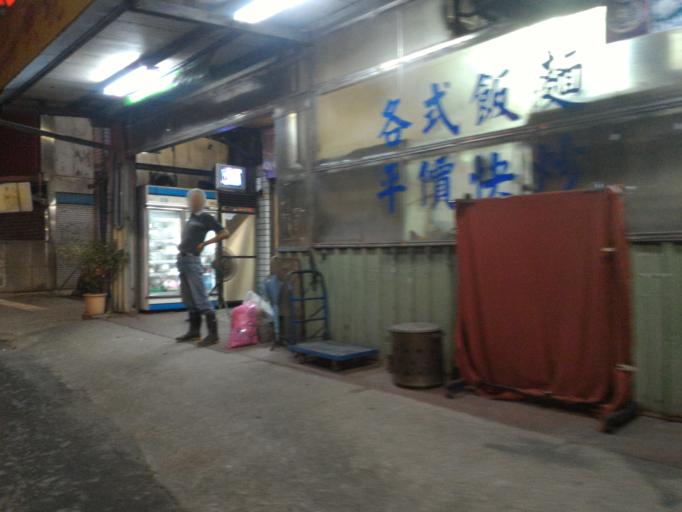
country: TW
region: Taipei
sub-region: Taipei
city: Banqiao
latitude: 24.9603
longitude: 121.4046
